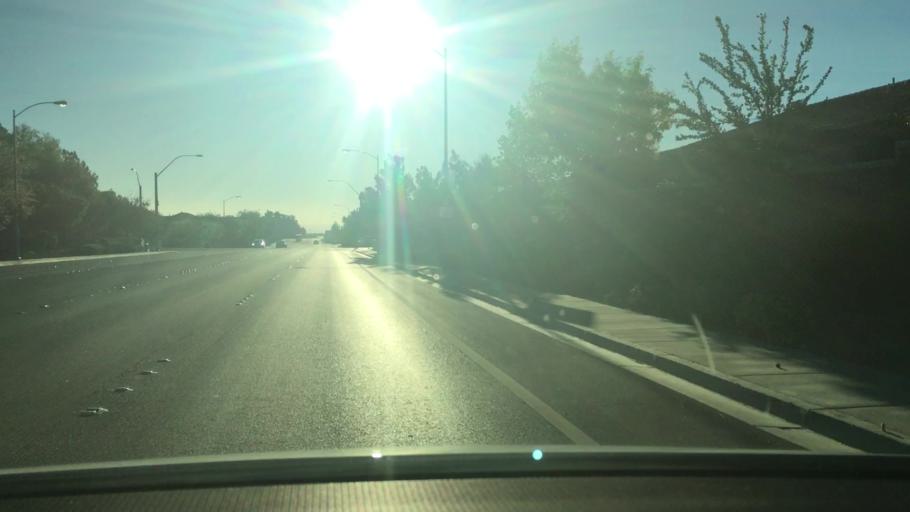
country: US
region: Nevada
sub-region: Clark County
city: Summerlin South
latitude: 36.0776
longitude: -115.3082
